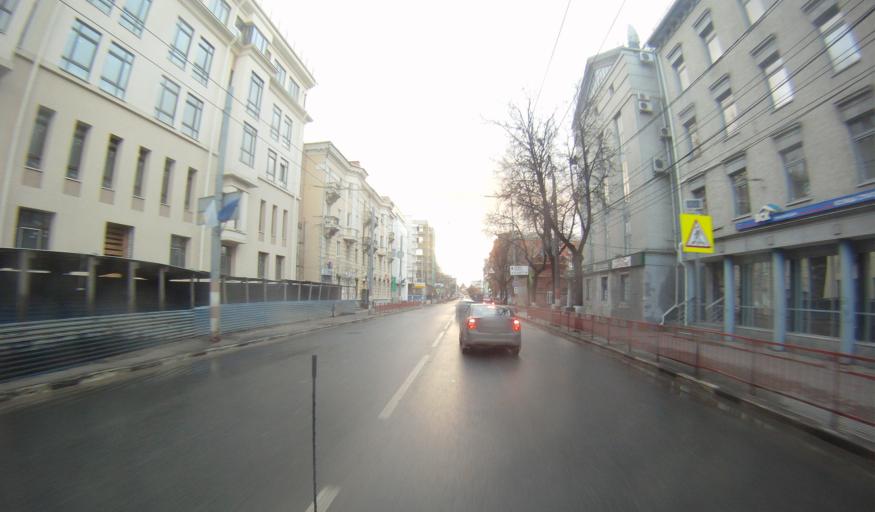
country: RU
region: Nizjnij Novgorod
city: Nizhniy Novgorod
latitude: 56.3200
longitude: 44.0139
